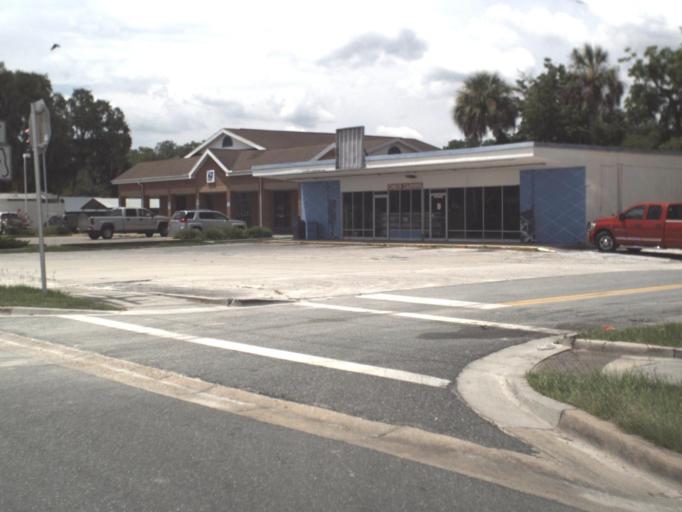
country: US
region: Florida
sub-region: Lafayette County
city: Mayo
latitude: 29.9598
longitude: -82.9296
